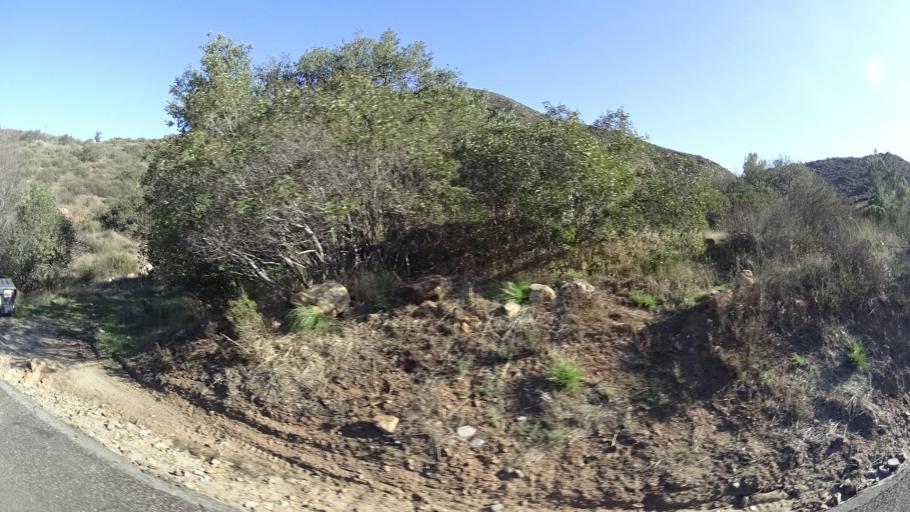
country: MX
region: Baja California
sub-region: Tijuana
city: Villa del Campo
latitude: 32.6233
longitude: -116.7491
